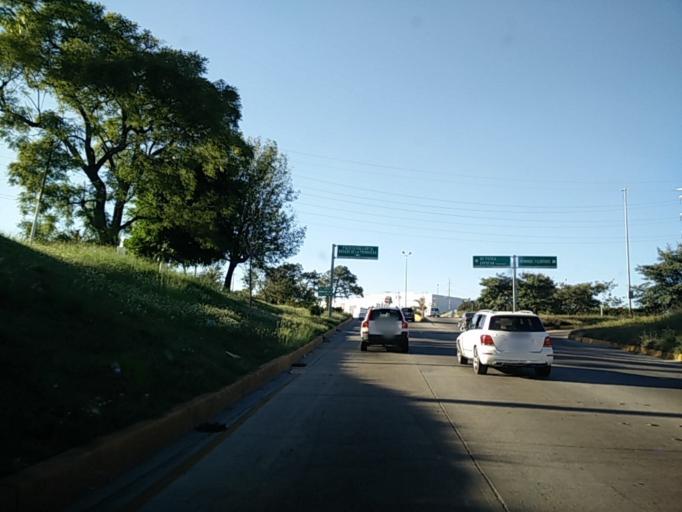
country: MX
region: Jalisco
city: Guadalajara
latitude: 20.6766
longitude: -103.4147
